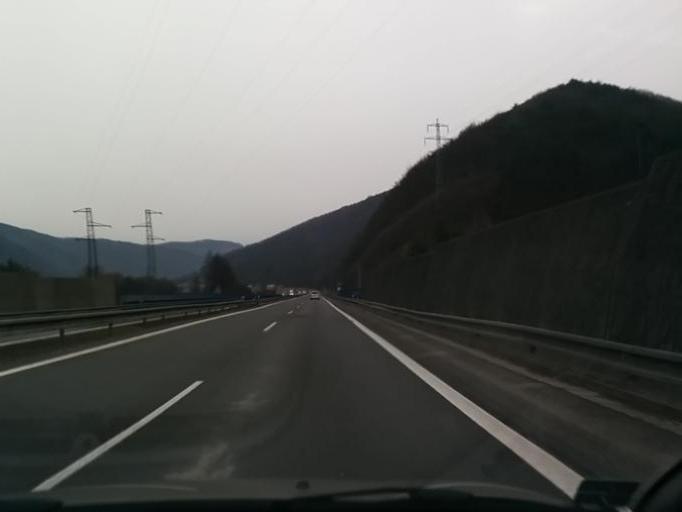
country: SK
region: Banskobystricky
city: Ziar nad Hronom
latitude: 48.5852
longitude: 18.9541
